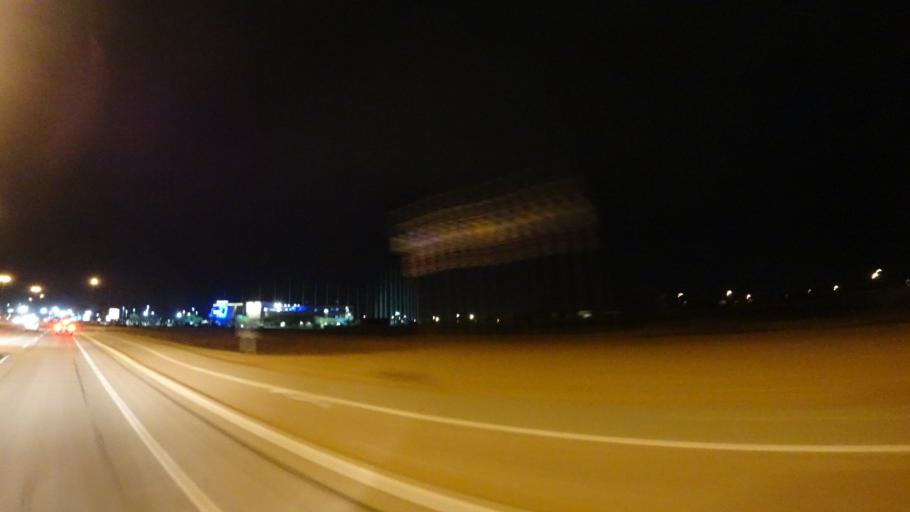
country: US
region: Arizona
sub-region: Maricopa County
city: Gilbert
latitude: 33.3179
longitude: -111.7427
